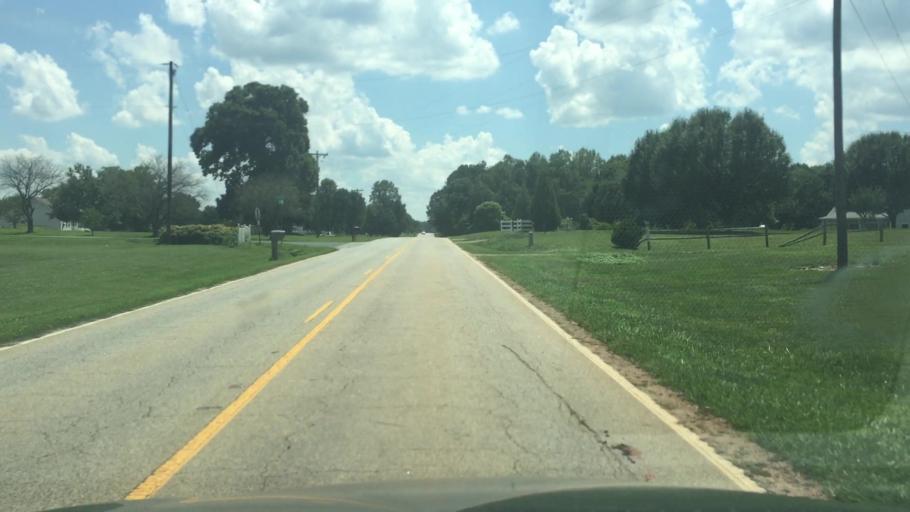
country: US
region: North Carolina
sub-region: Rowan County
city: China Grove
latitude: 35.6257
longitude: -80.6466
